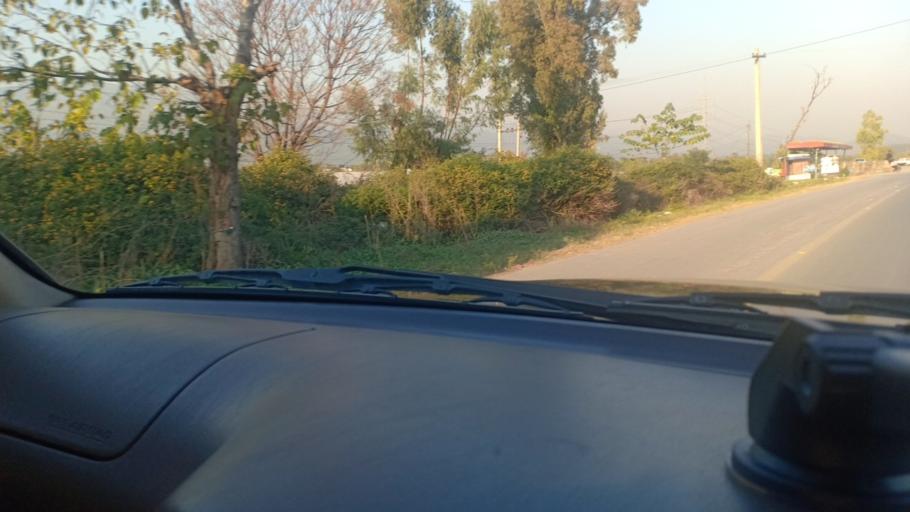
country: PK
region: Islamabad
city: Islamabad
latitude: 33.7290
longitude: 73.1436
